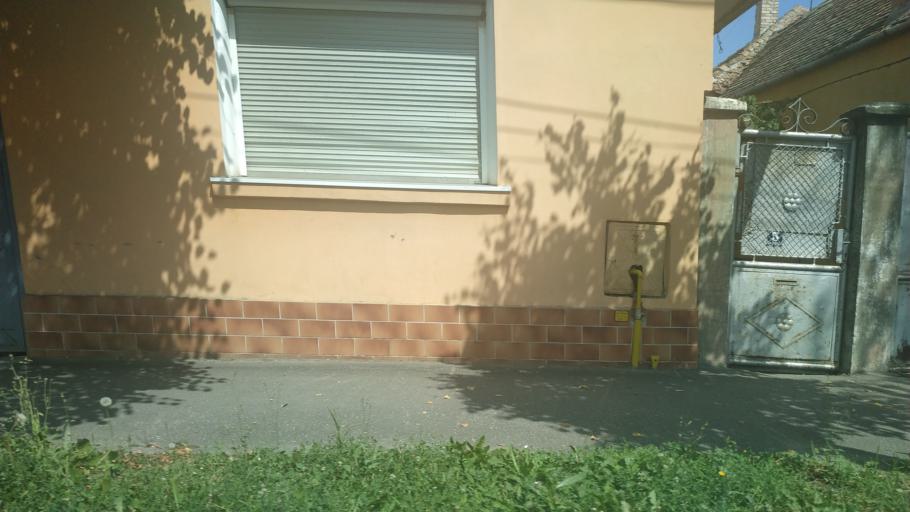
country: RO
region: Brasov
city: Fogarasch
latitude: 45.8415
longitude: 24.9658
